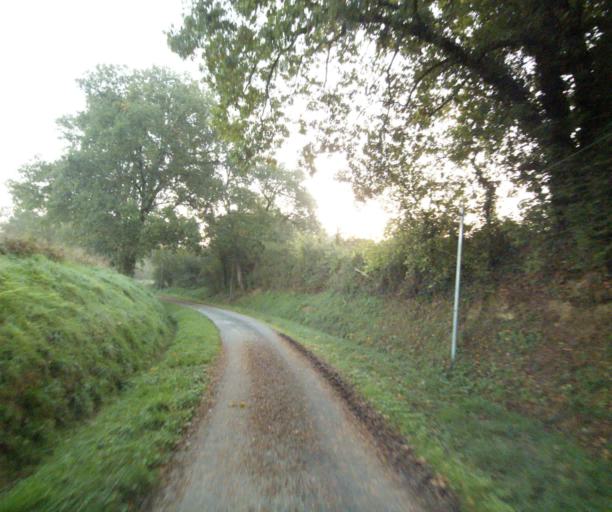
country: FR
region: Midi-Pyrenees
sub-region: Departement du Gers
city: Gondrin
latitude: 43.7962
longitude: 0.2205
